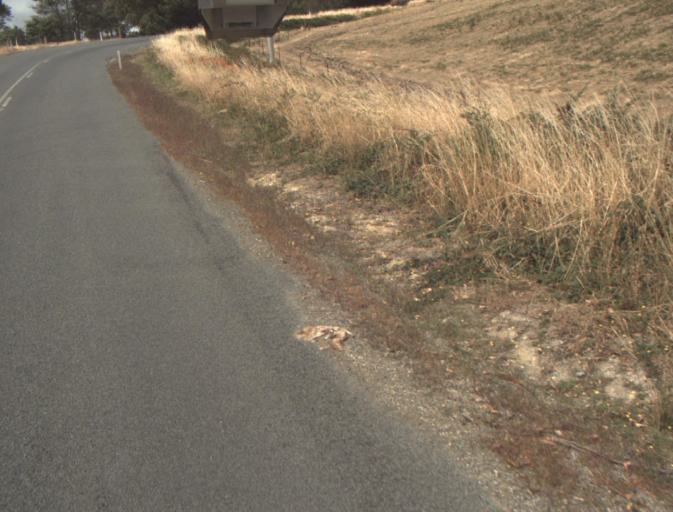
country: AU
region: Tasmania
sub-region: Launceston
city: Mayfield
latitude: -41.2011
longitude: 147.2178
